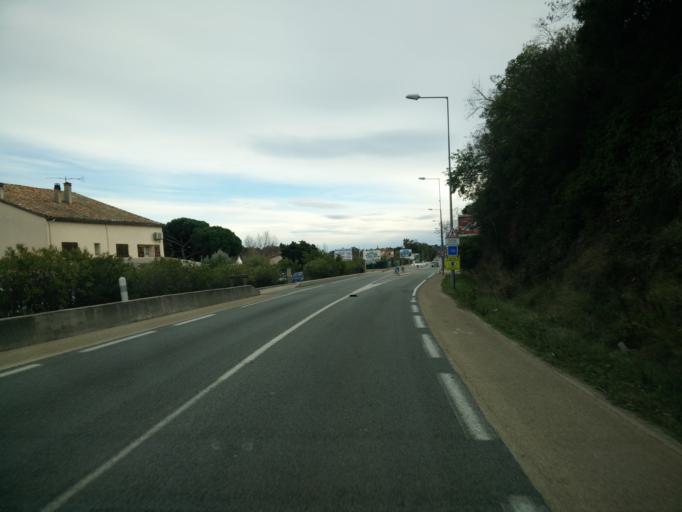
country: FR
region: Provence-Alpes-Cote d'Azur
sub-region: Departement du Var
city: Frejus
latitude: 43.4115
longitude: 6.7071
